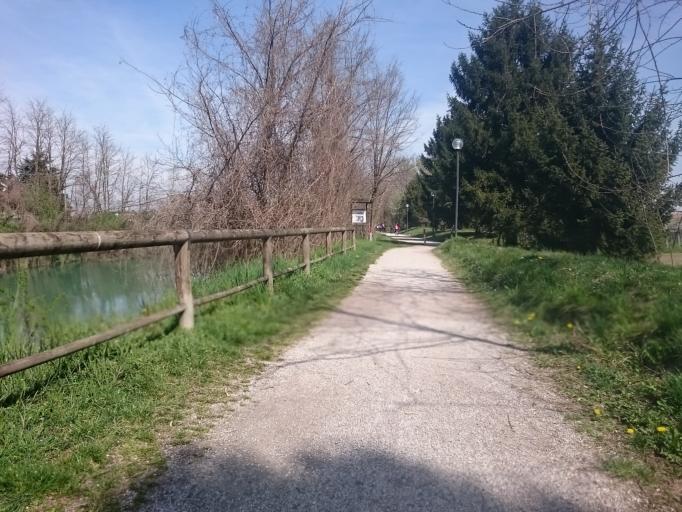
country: IT
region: Veneto
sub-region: Provincia di Padova
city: Limena
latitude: 45.4686
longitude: 11.8376
